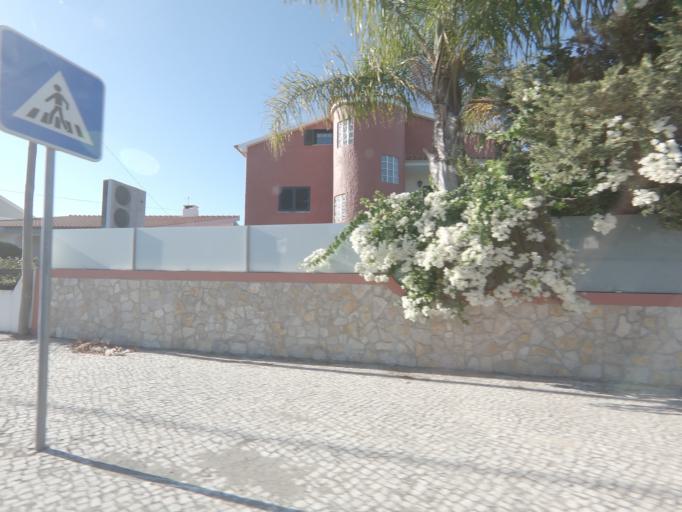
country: PT
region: Setubal
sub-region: Palmela
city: Quinta do Anjo
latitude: 38.5677
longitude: -8.9329
